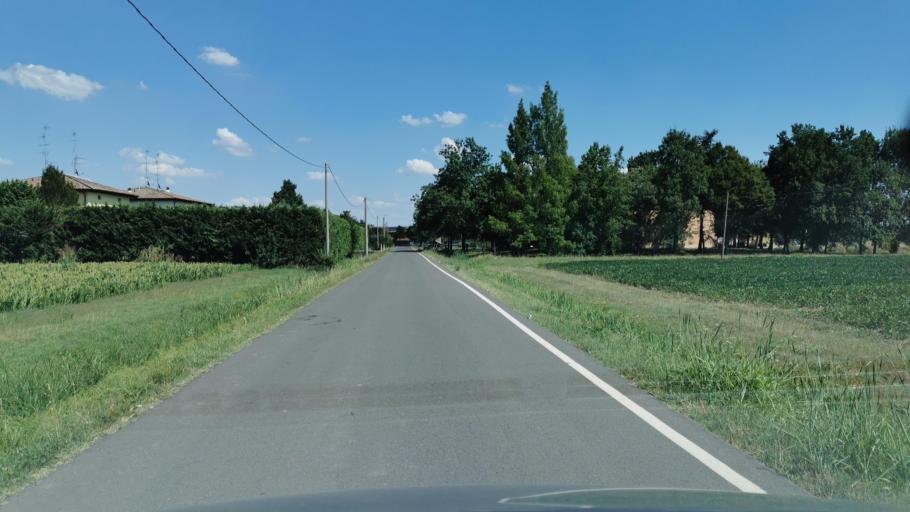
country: IT
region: Emilia-Romagna
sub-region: Provincia di Modena
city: Limidi
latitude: 44.7825
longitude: 10.9160
